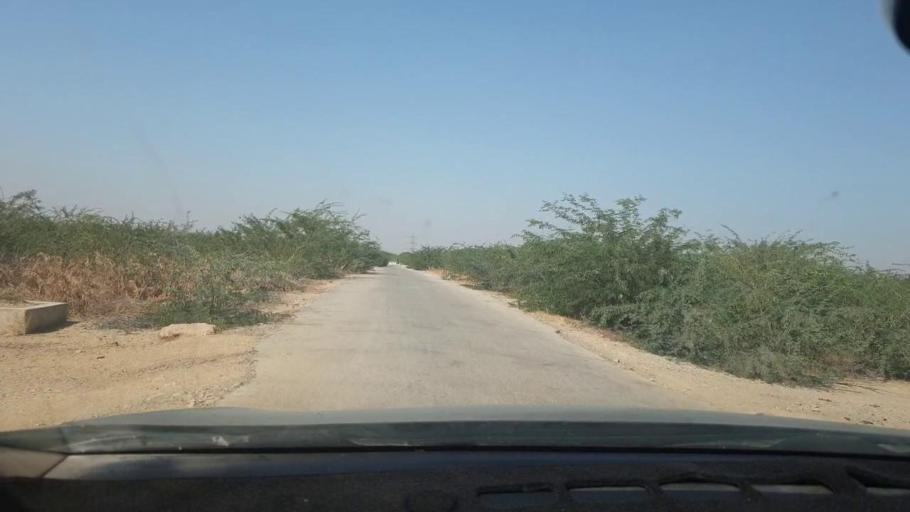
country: PK
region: Sindh
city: Malir Cantonment
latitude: 25.1601
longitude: 67.1631
